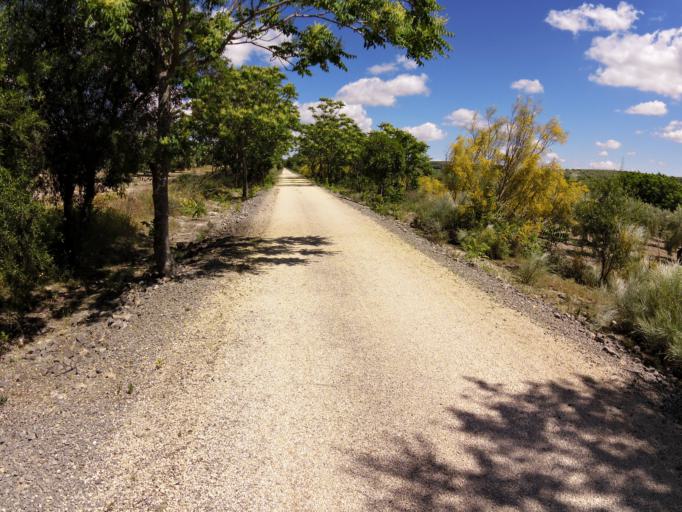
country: ES
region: Andalusia
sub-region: Provincia de Jaen
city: Alcaudete
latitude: 37.6527
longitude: -4.0616
